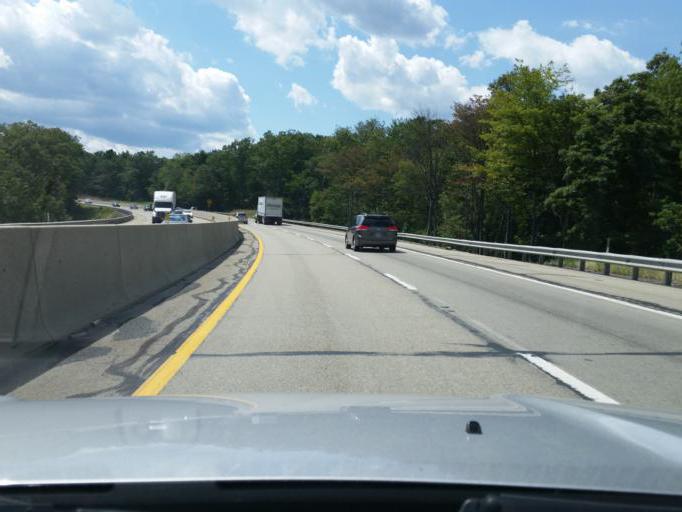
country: US
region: Pennsylvania
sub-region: Fulton County
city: McConnellsburg
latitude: 40.0449
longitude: -78.0205
